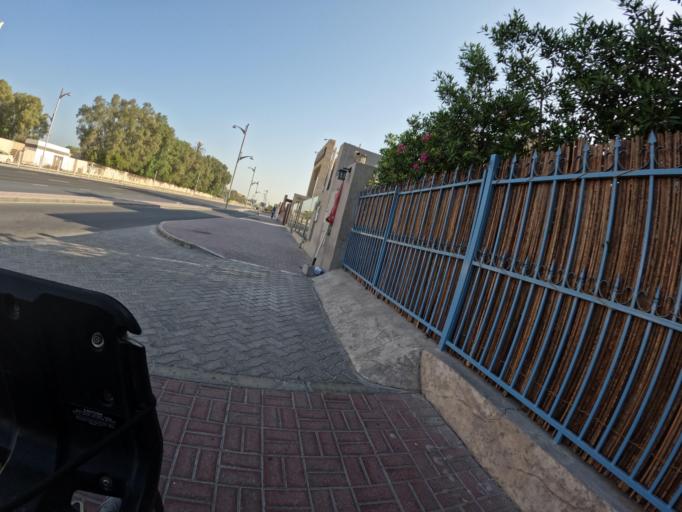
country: AE
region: Dubai
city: Dubai
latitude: 25.1983
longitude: 55.2384
